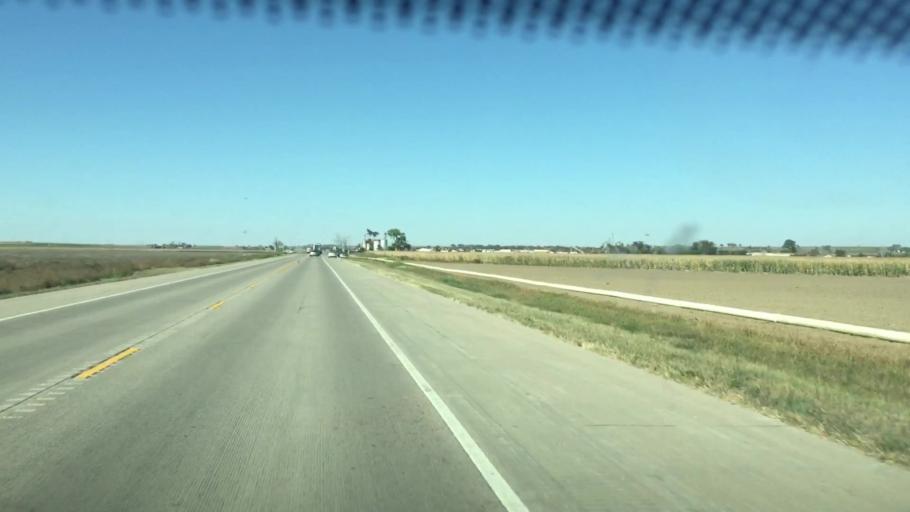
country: US
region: Colorado
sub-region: Prowers County
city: Lamar
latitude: 38.1364
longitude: -102.7237
